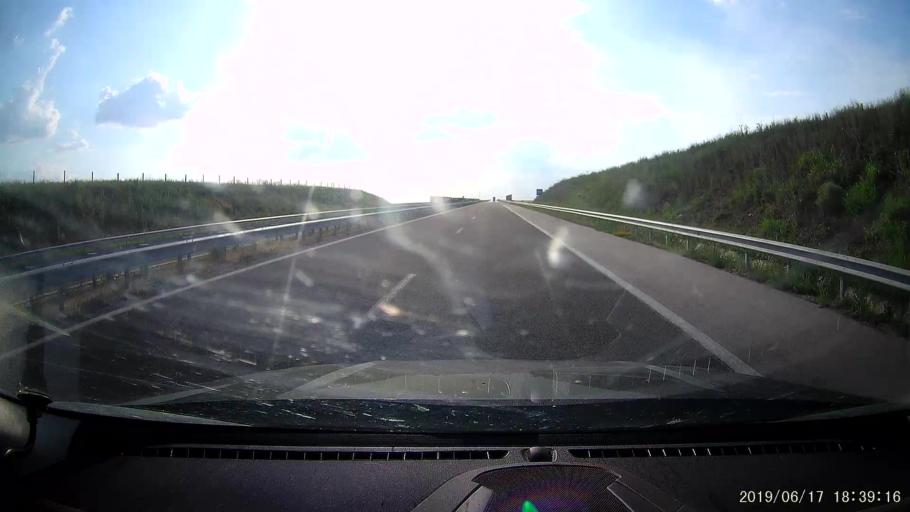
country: BG
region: Stara Zagora
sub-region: Obshtina Chirpan
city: Chirpan
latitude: 42.1435
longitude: 25.3123
